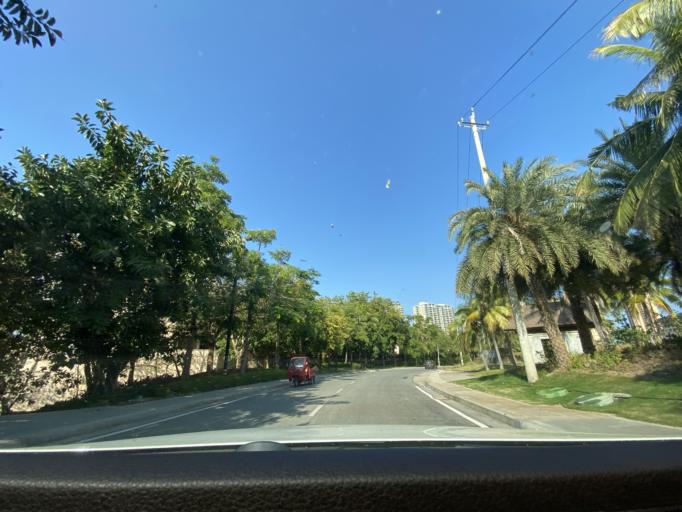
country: CN
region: Hainan
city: Yingzhou
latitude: 18.4110
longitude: 109.8819
